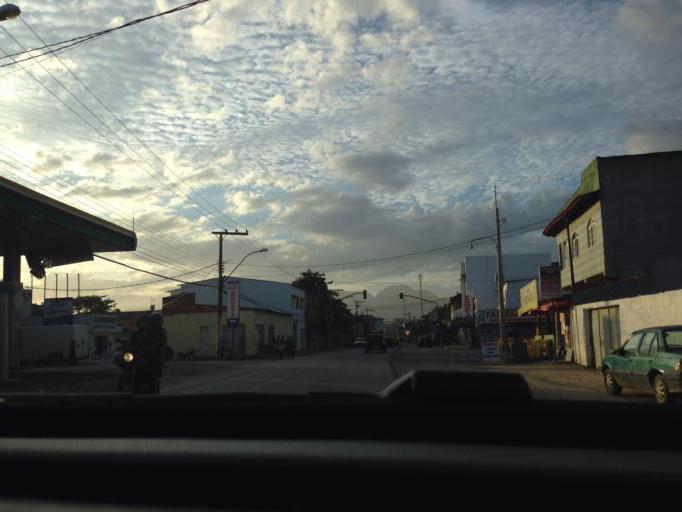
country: BR
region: Espirito Santo
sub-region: Guarapari
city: Guarapari
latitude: -20.6240
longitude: -40.4500
